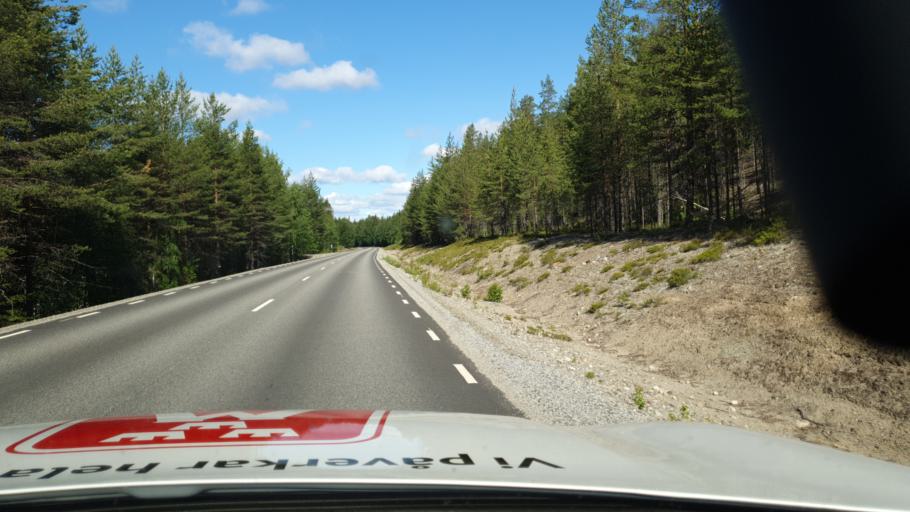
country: SE
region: Vaesterbotten
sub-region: Norsjo Kommun
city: Norsjoe
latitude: 64.6874
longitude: 19.2186
